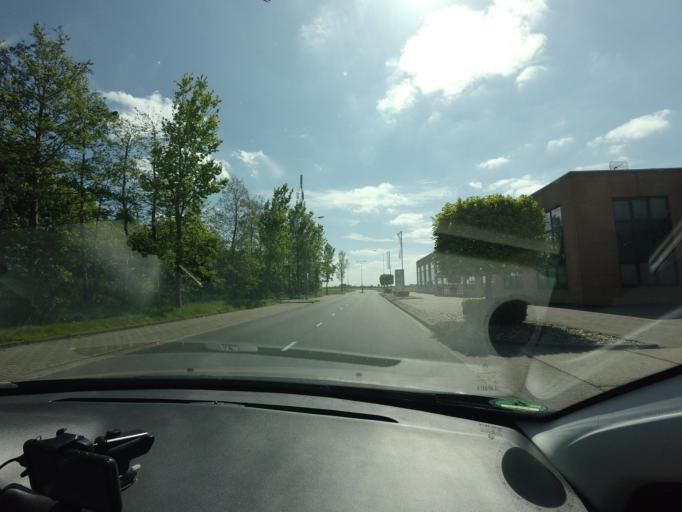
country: NL
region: North Holland
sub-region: Gemeente Beemster
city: Halfweg
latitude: 52.5483
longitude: 4.8994
